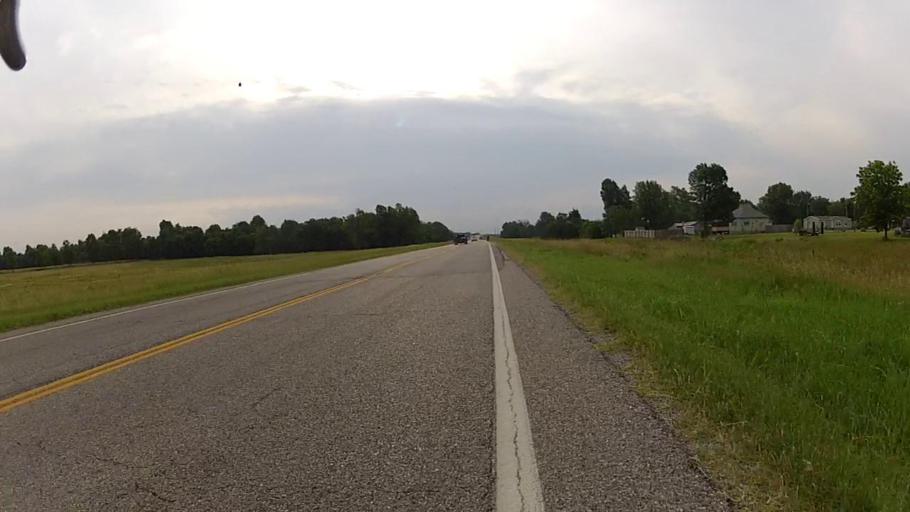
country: US
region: Kansas
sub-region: Cherokee County
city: Columbus
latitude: 37.1785
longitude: -94.8474
